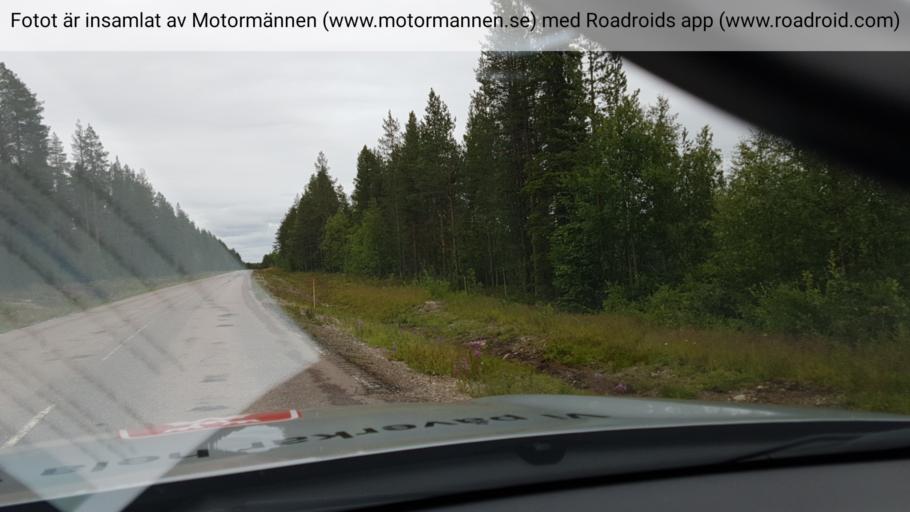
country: SE
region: Norrbotten
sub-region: Overkalix Kommun
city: OEverkalix
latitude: 67.0642
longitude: 22.2626
